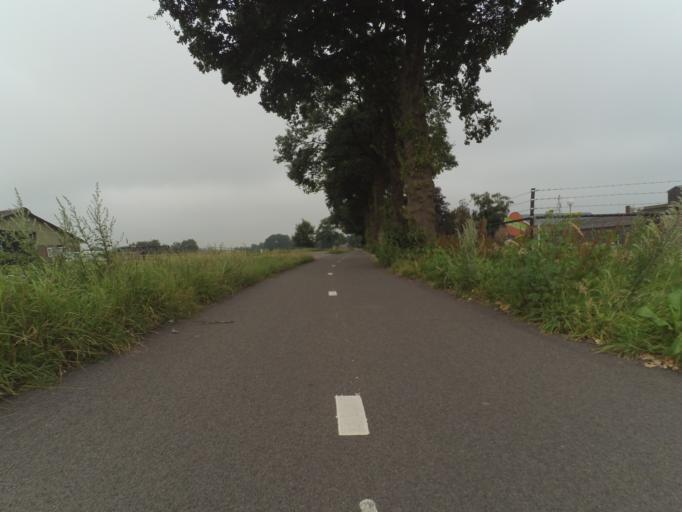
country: NL
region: Gelderland
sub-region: Gemeente Barneveld
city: Barneveld
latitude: 52.1217
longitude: 5.5490
